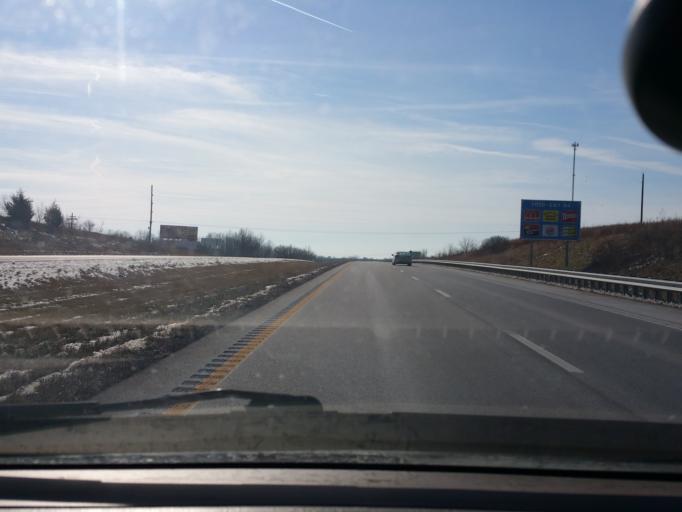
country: US
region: Missouri
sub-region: Clinton County
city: Cameron
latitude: 39.7661
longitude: -94.2157
